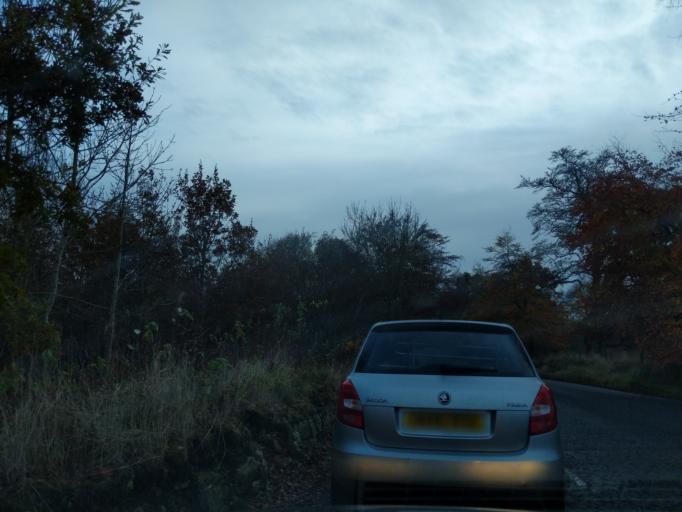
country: GB
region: Scotland
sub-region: West Lothian
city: Bathgate
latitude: 55.9372
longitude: -3.6230
